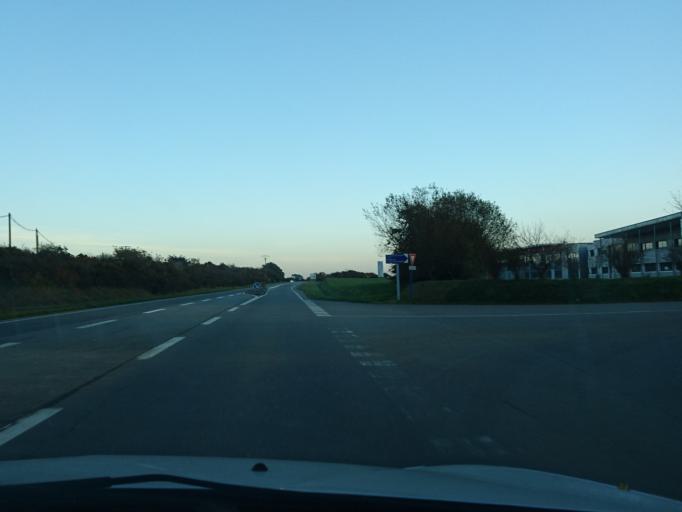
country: FR
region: Brittany
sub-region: Departement du Finistere
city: Lanrivoare
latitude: 48.4709
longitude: -4.6458
